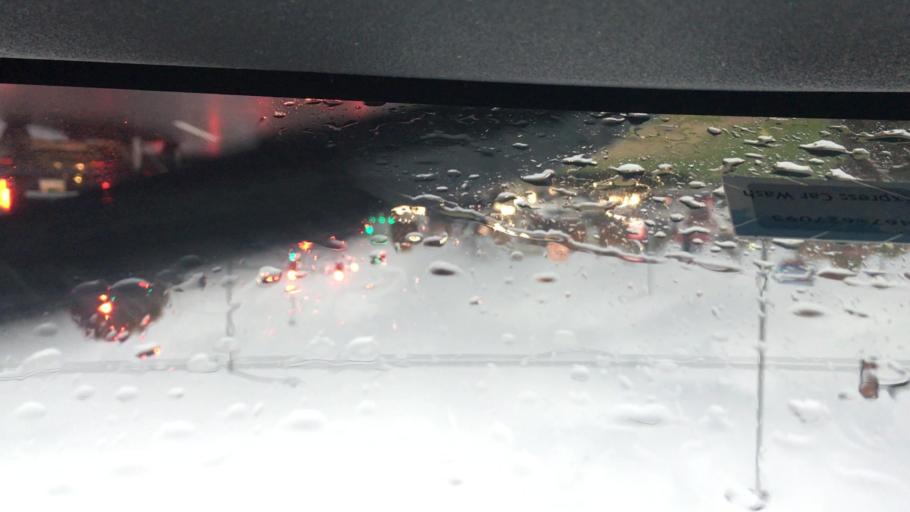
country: US
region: Illinois
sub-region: McLean County
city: Bloomington
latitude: 40.4882
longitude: -88.9535
